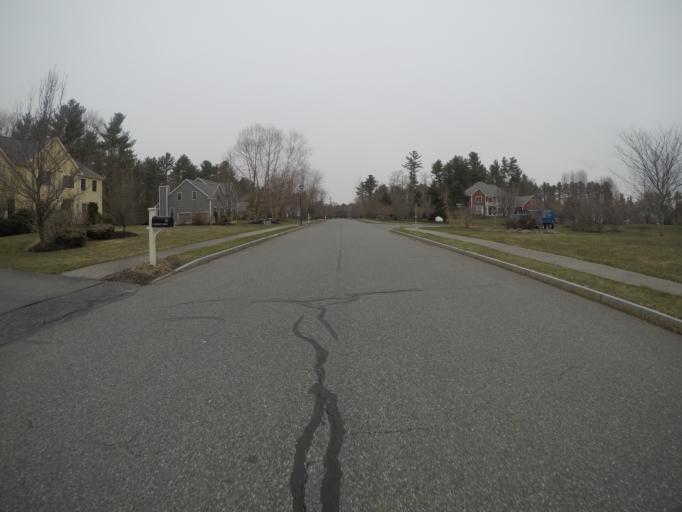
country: US
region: Massachusetts
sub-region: Bristol County
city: Easton
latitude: 42.0179
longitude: -71.1126
